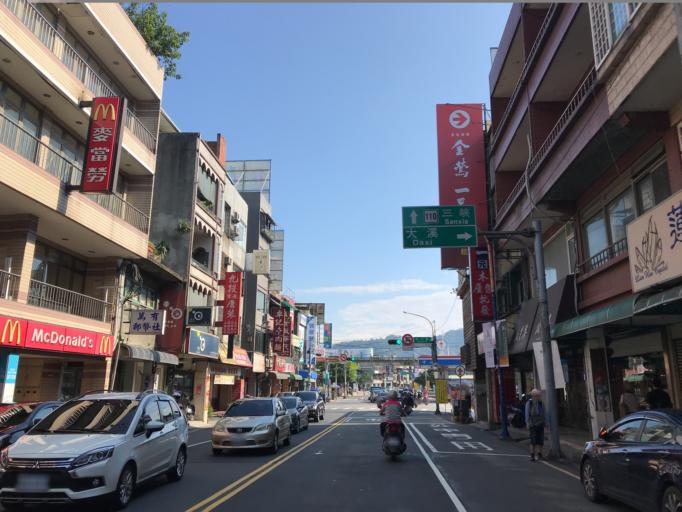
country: TW
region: Taiwan
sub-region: Taoyuan
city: Taoyuan
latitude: 24.9512
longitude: 121.3521
